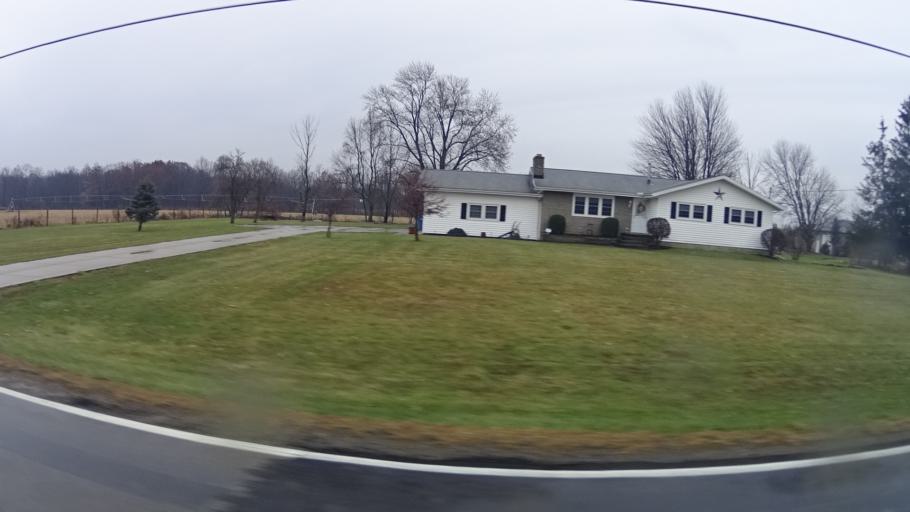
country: US
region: Ohio
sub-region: Lorain County
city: Lagrange
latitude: 41.2603
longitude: -82.1576
